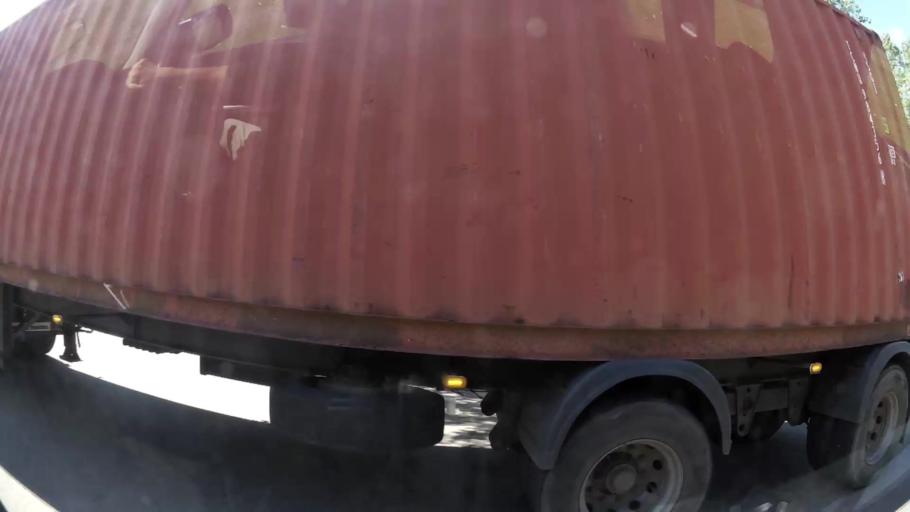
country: UY
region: Montevideo
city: Montevideo
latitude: -34.8604
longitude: -56.1460
